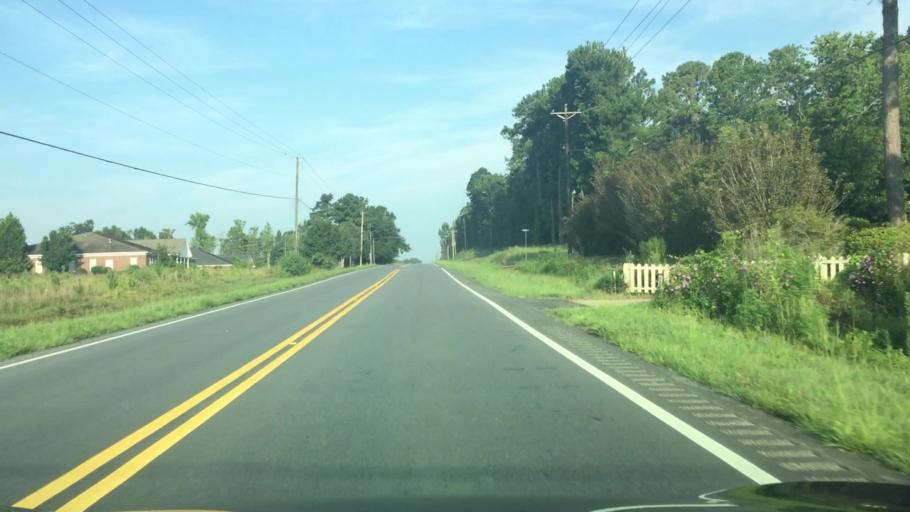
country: US
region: Alabama
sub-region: Covington County
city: Andalusia
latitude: 31.2782
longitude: -86.4869
